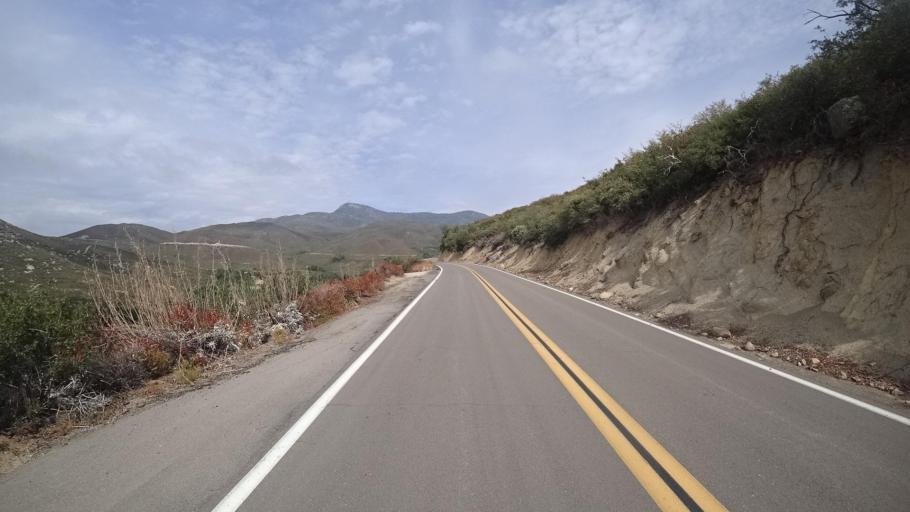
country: US
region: California
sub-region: San Diego County
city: Descanso
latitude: 32.9157
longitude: -116.6386
